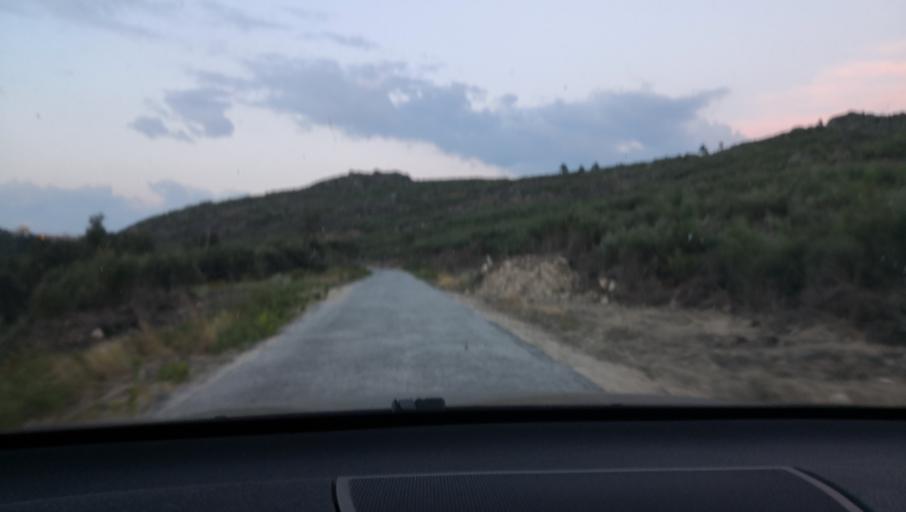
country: PT
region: Vila Real
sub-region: Sabrosa
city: Sabrosa
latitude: 41.2829
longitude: -7.6238
